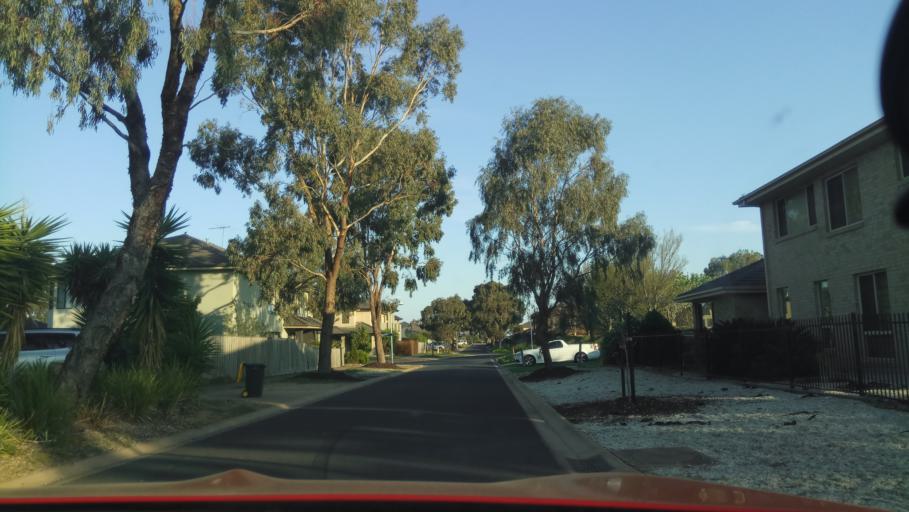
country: AU
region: Victoria
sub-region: Hobsons Bay
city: Altona Meadows
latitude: -37.8892
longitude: 144.7696
